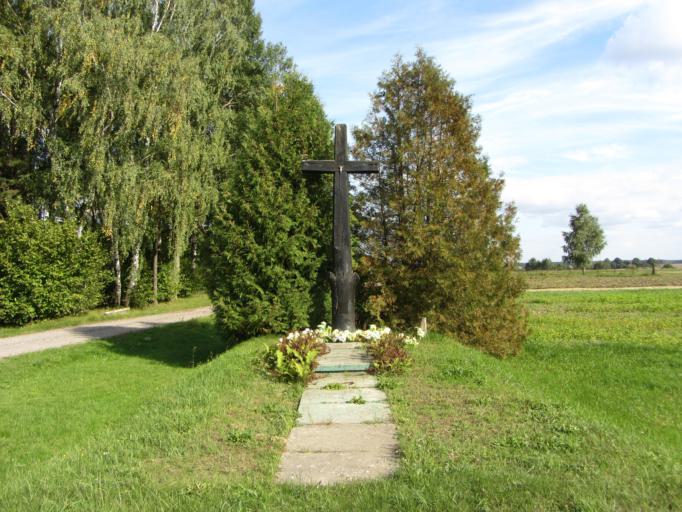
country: BY
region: Grodnenskaya
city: Voranava
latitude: 54.2417
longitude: 25.2009
